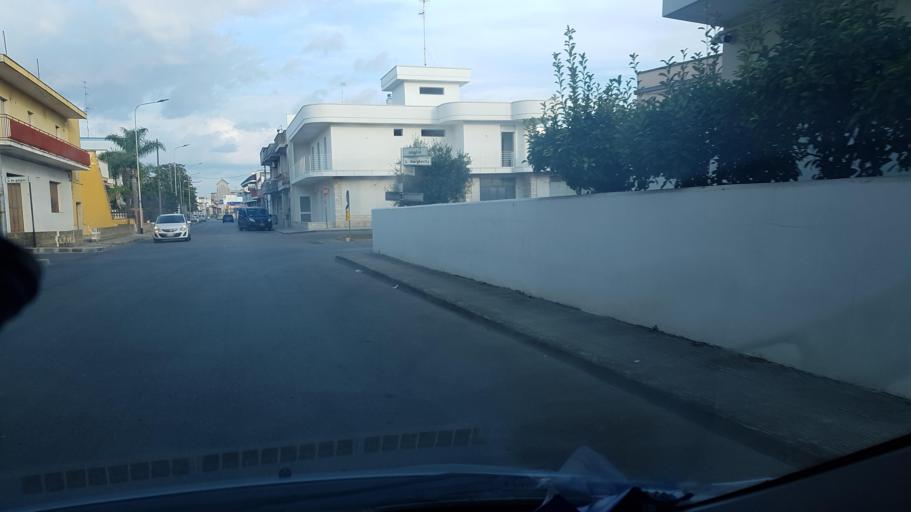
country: IT
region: Apulia
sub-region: Provincia di Lecce
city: Carmiano
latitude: 40.3452
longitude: 18.0371
